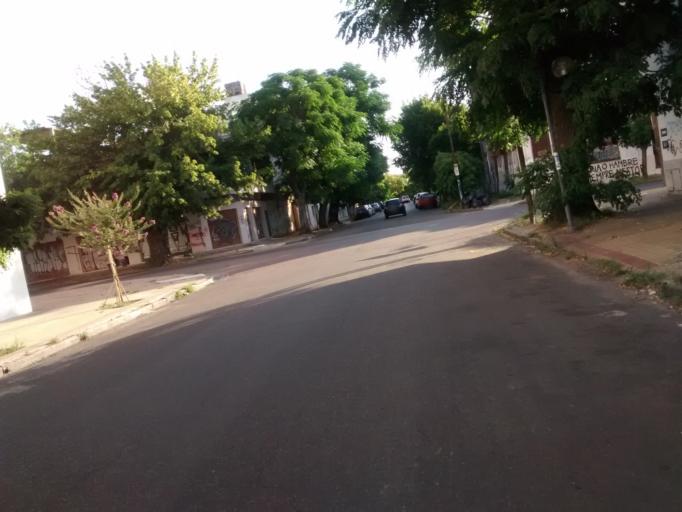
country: AR
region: Buenos Aires
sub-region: Partido de La Plata
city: La Plata
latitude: -34.9231
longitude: -57.9358
